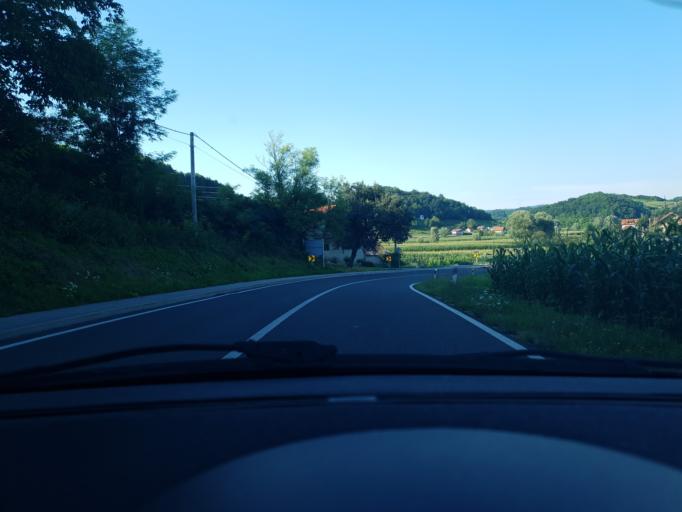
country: HR
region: Krapinsko-Zagorska
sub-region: Grad Krapina
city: Krapina
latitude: 46.1134
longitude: 15.9060
